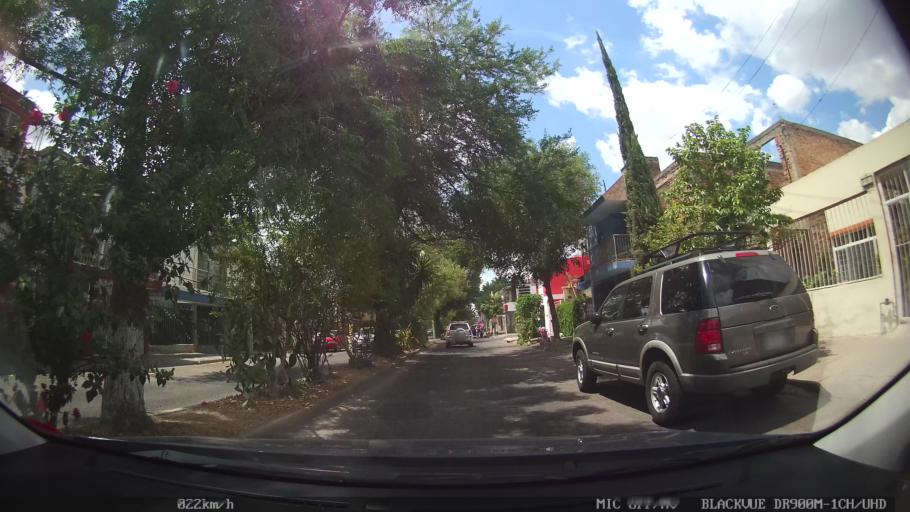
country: MX
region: Jalisco
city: Tlaquepaque
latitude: 20.6500
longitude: -103.2833
